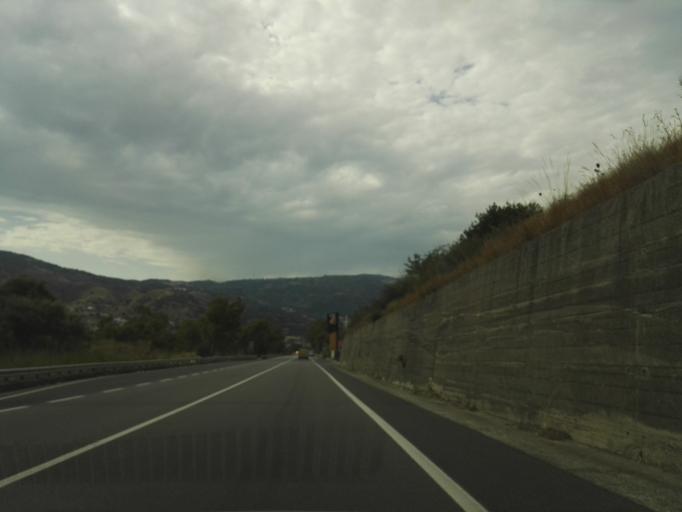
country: IT
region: Calabria
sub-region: Provincia di Catanzaro
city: Soverato Superiore
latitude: 38.6988
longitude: 16.5366
